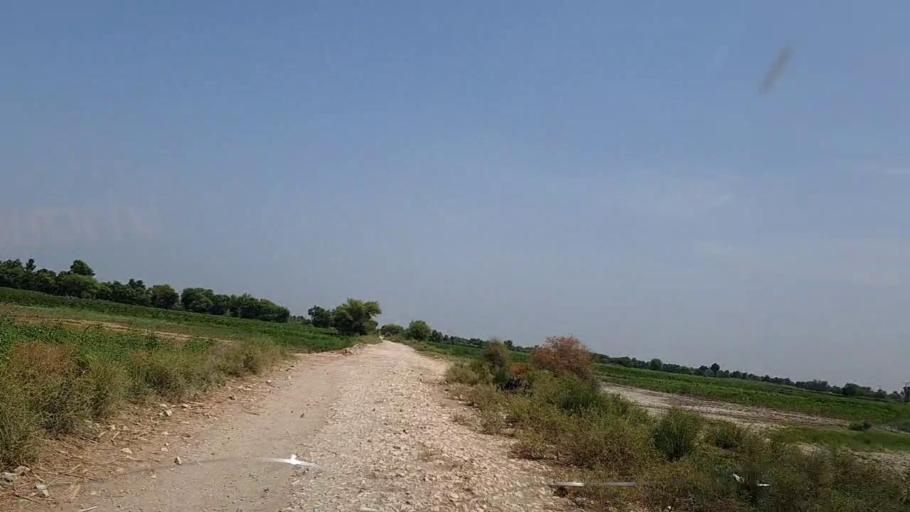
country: PK
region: Sindh
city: Adilpur
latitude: 27.8375
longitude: 69.2809
